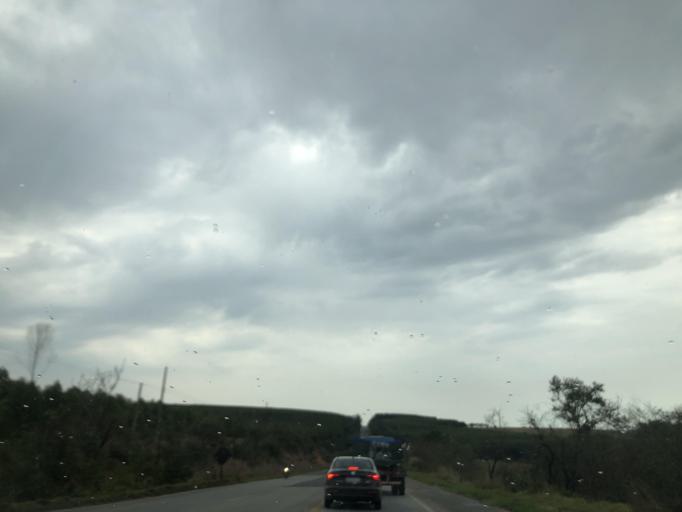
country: BR
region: Sao Paulo
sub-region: Salto De Pirapora
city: Salto de Pirapora
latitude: -23.6833
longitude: -47.6060
